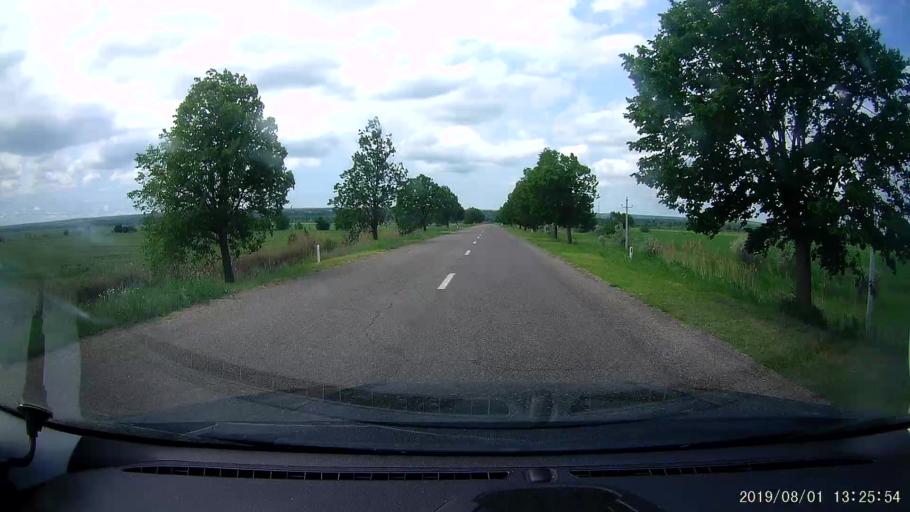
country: RO
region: Galati
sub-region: Comuna Oancea
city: Oancea
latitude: 45.9144
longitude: 28.1425
